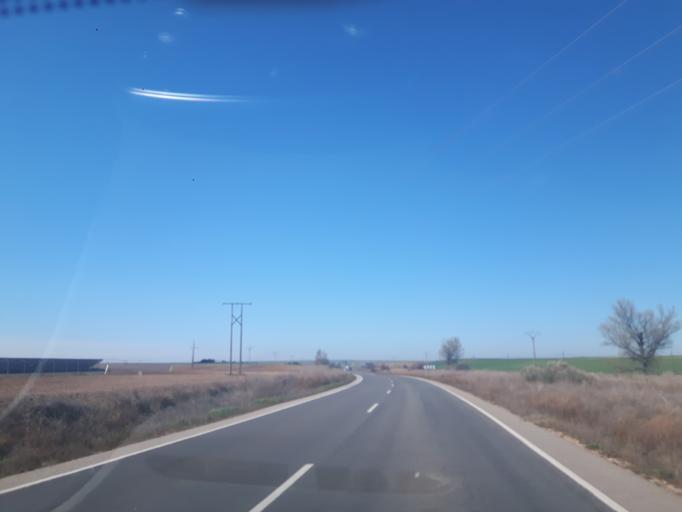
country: ES
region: Castille and Leon
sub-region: Provincia de Salamanca
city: Nava de Sotrobal
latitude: 40.8927
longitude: -5.2567
